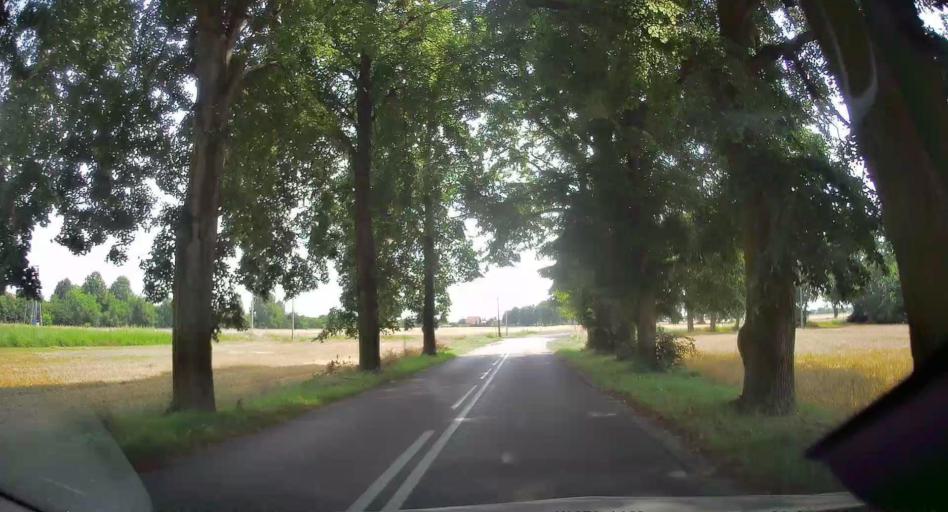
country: PL
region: Lodz Voivodeship
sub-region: Powiat tomaszowski
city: Lubochnia
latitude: 51.5689
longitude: 20.1044
